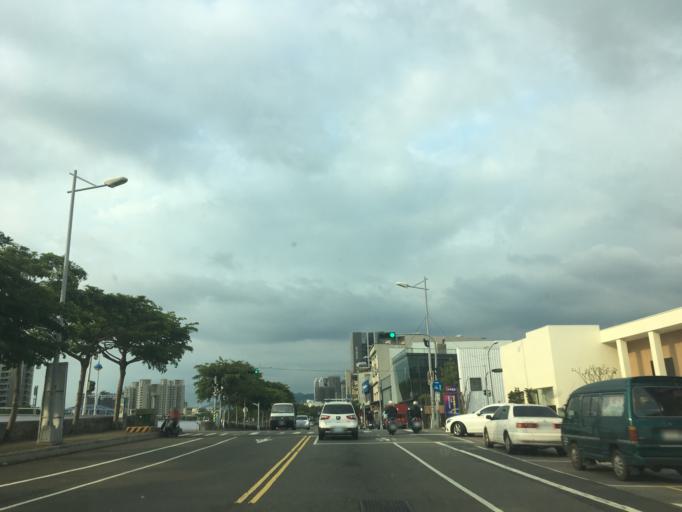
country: TW
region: Taiwan
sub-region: Taichung City
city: Taichung
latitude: 24.1528
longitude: 120.7026
